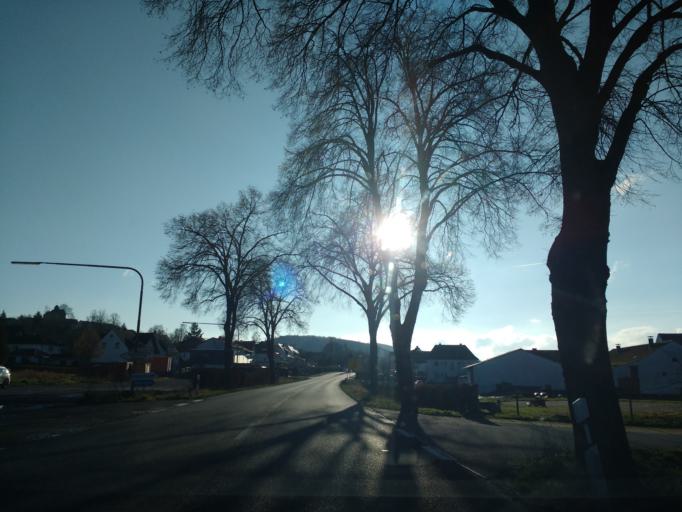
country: DE
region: Hesse
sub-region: Regierungsbezirk Kassel
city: Schrecksbach
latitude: 50.8580
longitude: 9.2904
